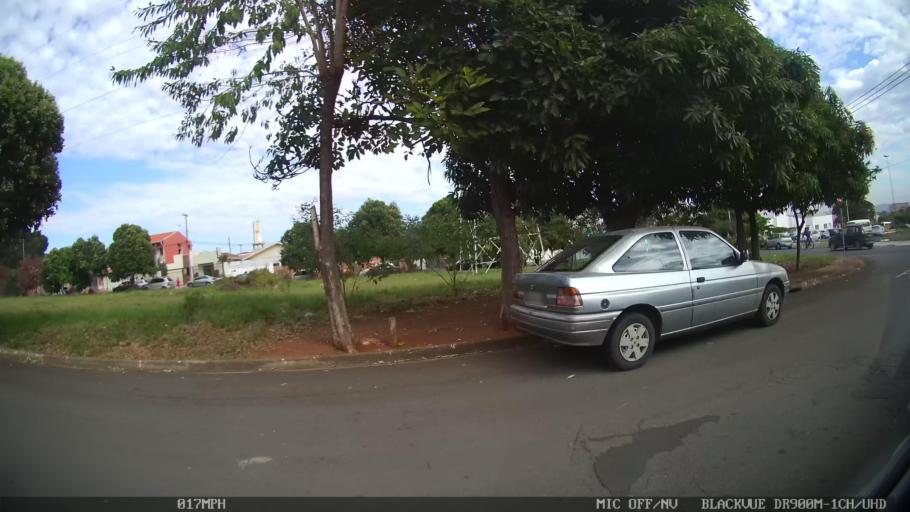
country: BR
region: Sao Paulo
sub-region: Americana
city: Americana
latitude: -22.7192
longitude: -47.3637
